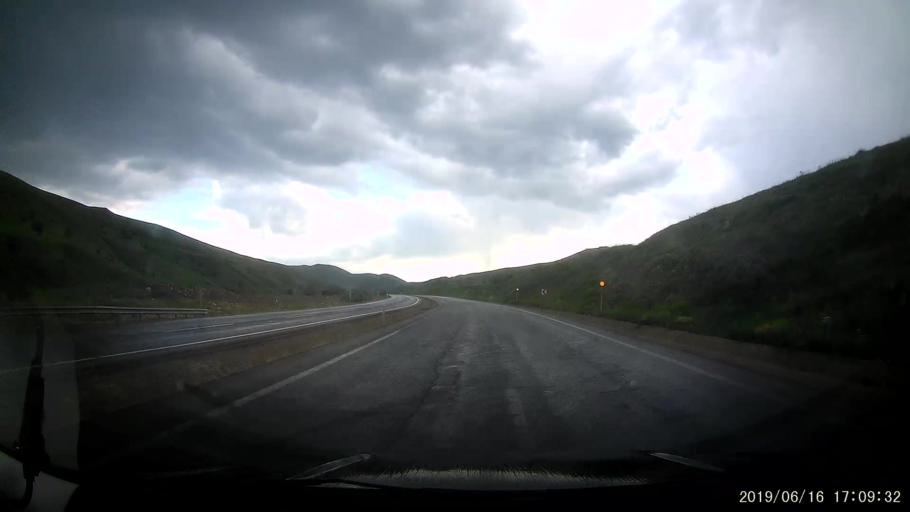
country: TR
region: Erzurum
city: Askale
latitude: 39.8937
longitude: 40.6487
